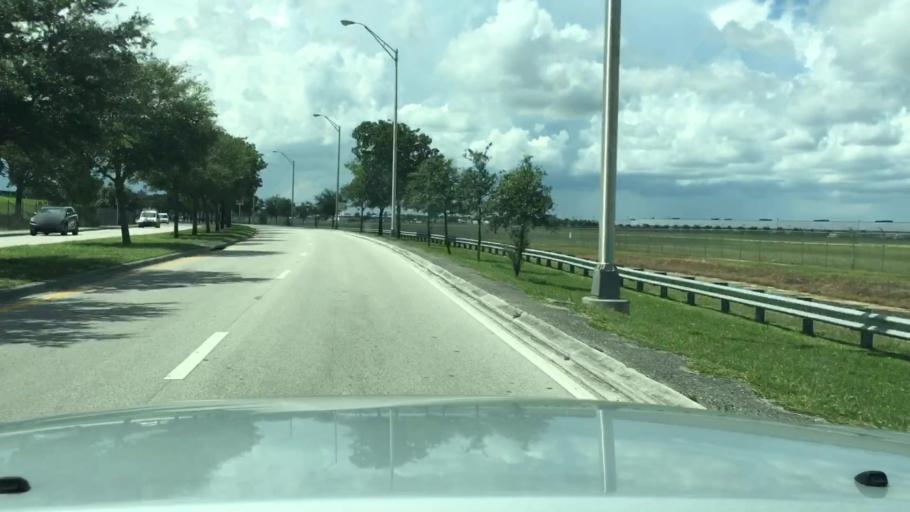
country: US
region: Florida
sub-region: Miami-Dade County
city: Miami Lakes
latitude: 25.8966
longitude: -80.2828
